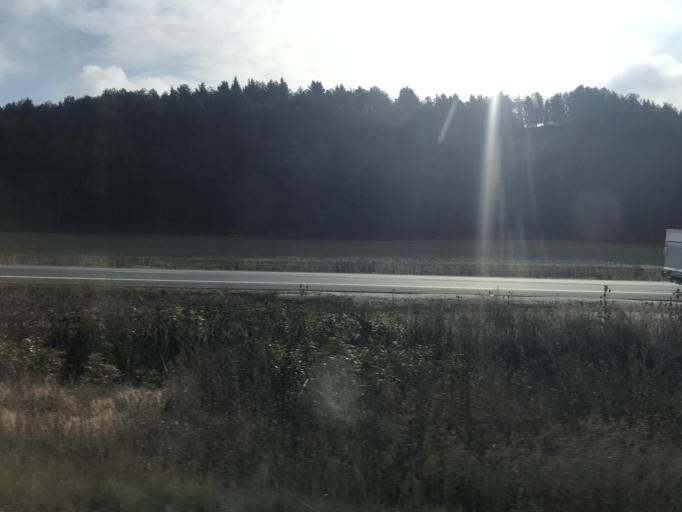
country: ES
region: Castille and Leon
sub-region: Provincia de Burgos
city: Pradanos de Bureba
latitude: 42.5108
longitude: -3.3411
